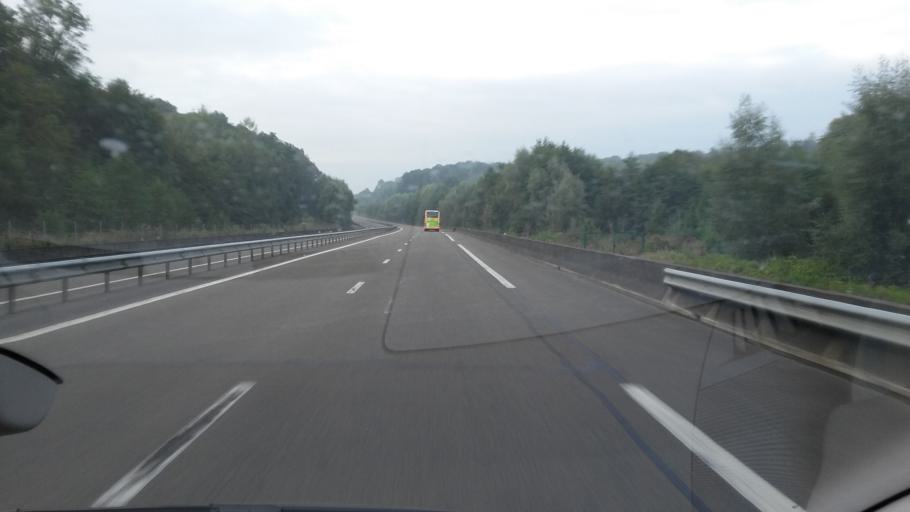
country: FR
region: Champagne-Ardenne
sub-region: Departement des Ardennes
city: Attigny
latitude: 49.6377
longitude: 4.5650
